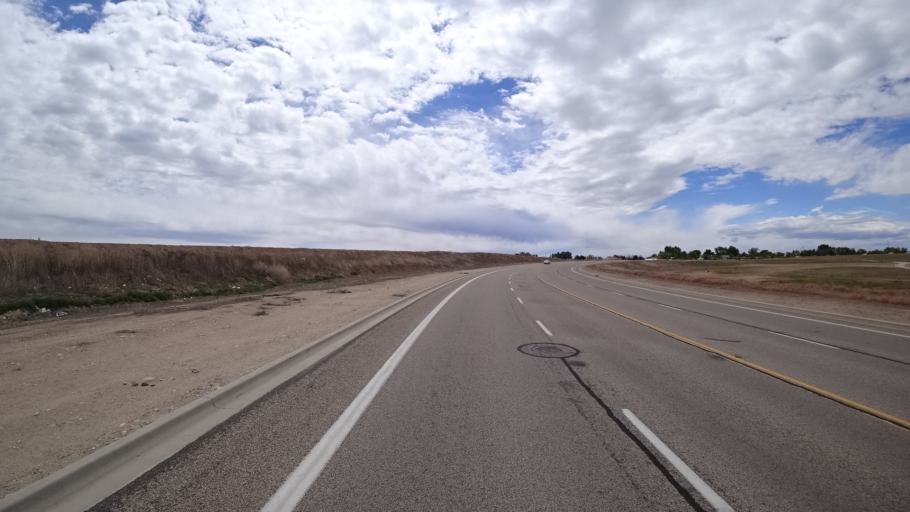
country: US
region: Idaho
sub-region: Ada County
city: Meridian
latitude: 43.5871
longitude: -116.4283
